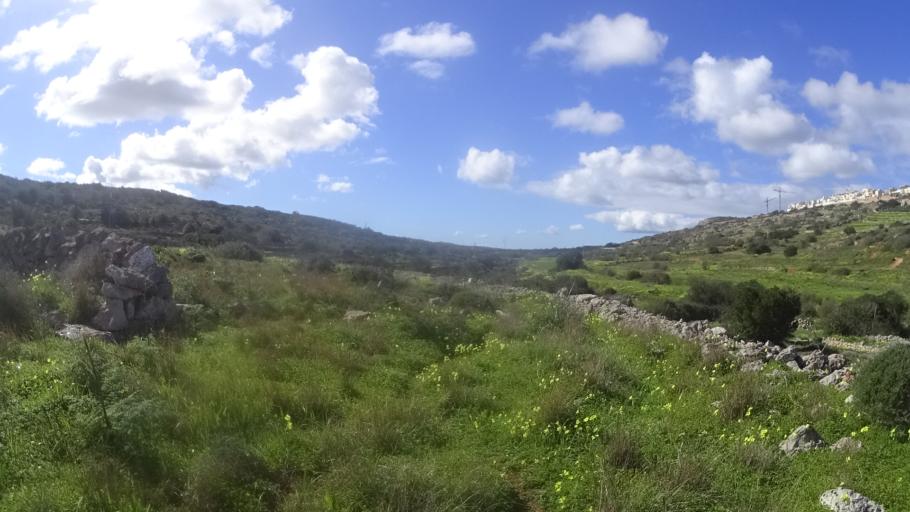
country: MT
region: Il-Mellieha
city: Mellieha
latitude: 35.9509
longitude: 14.3771
